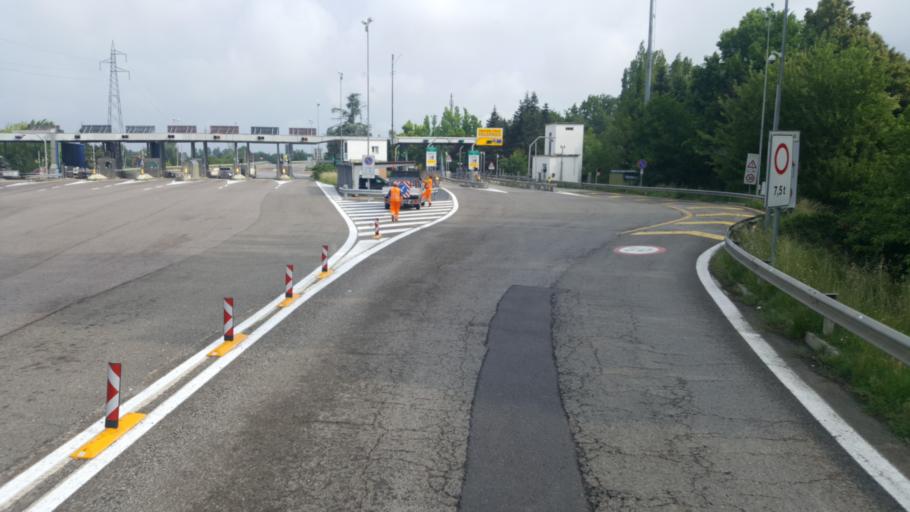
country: IT
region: Emilia-Romagna
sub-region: Provincia di Modena
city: San Vito
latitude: 44.5750
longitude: 10.9841
